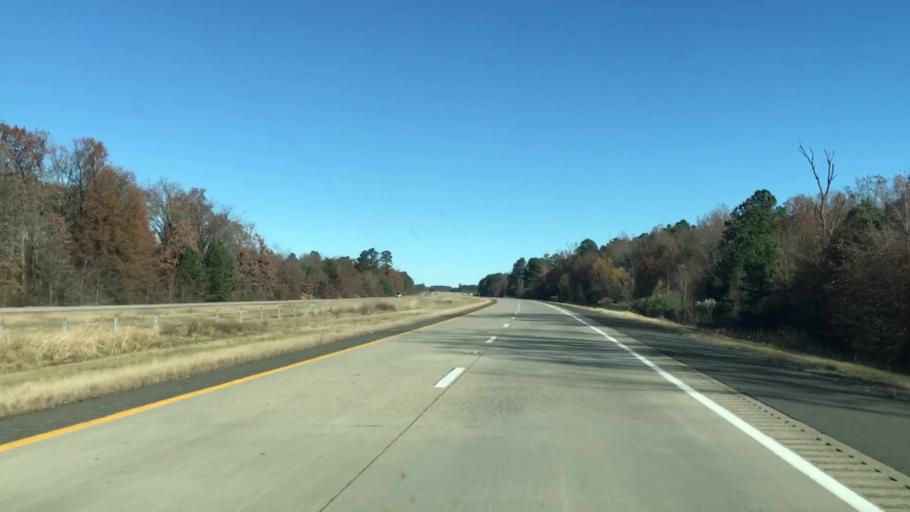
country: US
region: Texas
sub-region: Bowie County
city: Texarkana
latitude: 33.2130
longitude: -93.8737
